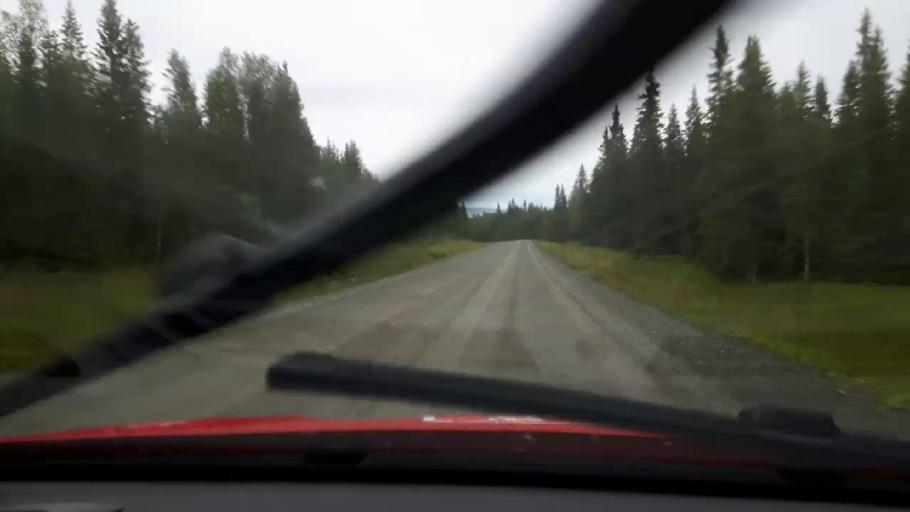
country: SE
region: Jaemtland
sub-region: Are Kommun
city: Are
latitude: 63.4494
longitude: 12.6595
